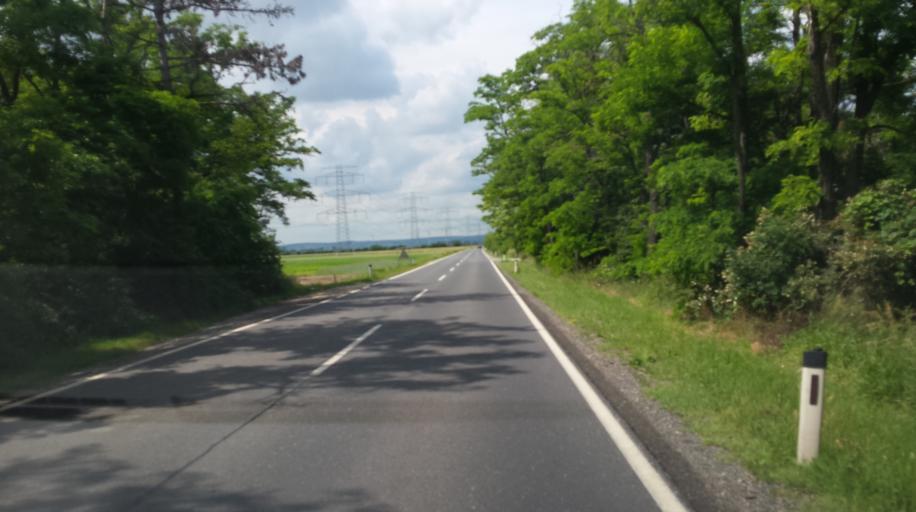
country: AT
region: Lower Austria
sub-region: Politischer Bezirk Ganserndorf
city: Aderklaa
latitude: 48.3063
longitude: 16.5401
